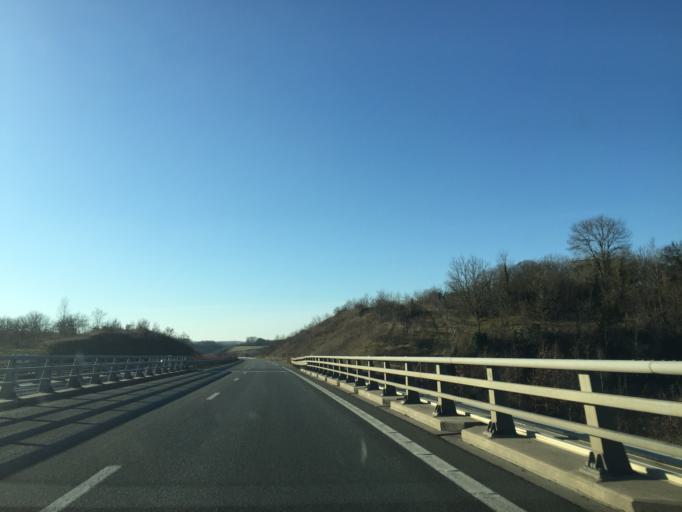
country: FR
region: Aquitaine
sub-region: Departement de la Dordogne
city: Thenon
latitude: 45.1553
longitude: 1.1204
